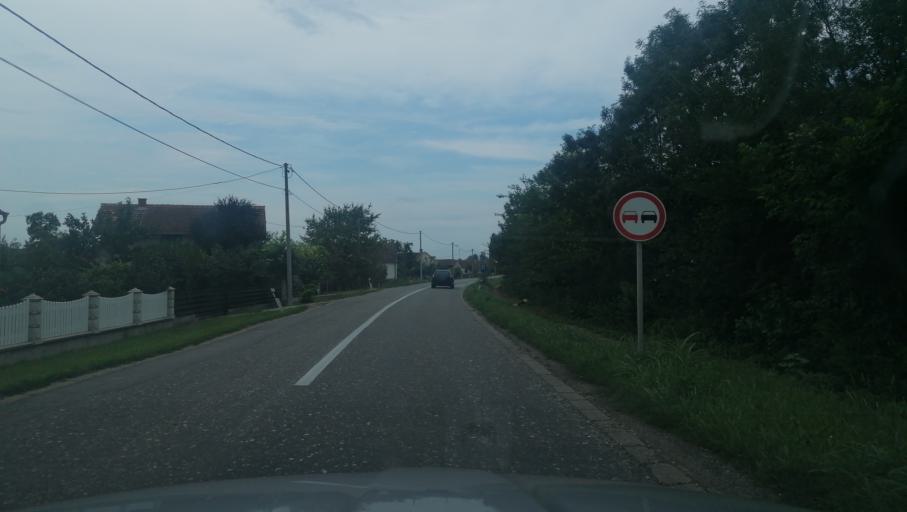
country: RS
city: Klenje
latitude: 44.8136
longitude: 19.4423
